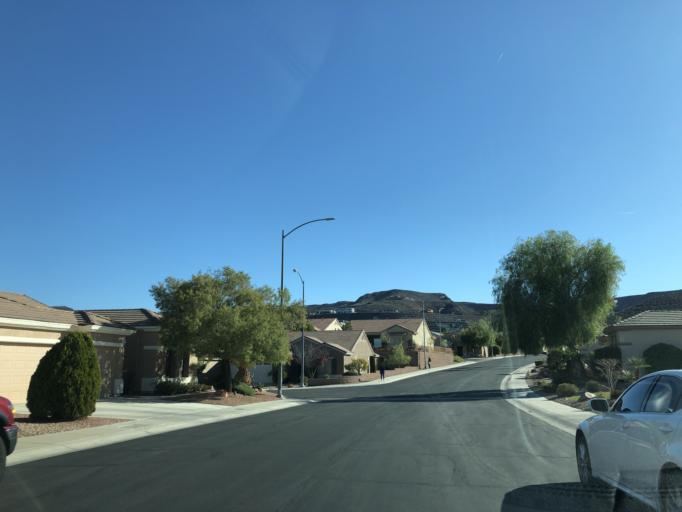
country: US
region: Nevada
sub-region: Clark County
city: Whitney
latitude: 36.0031
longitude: -115.0689
